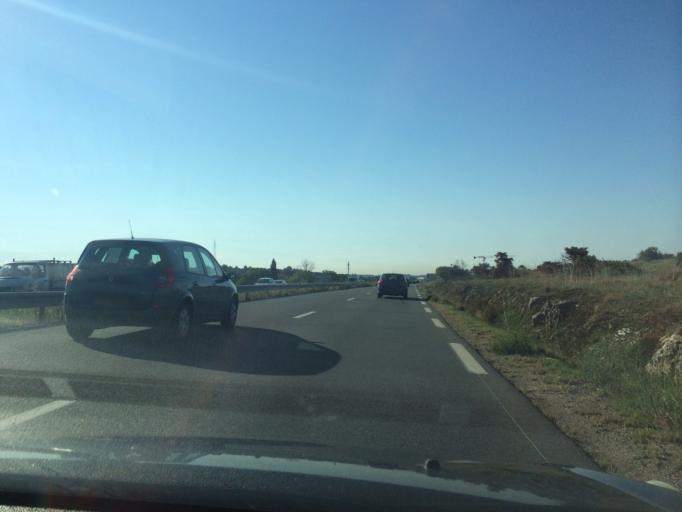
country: FR
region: Languedoc-Roussillon
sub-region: Departement de l'Herault
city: Grabels
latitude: 43.6282
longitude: 3.7818
